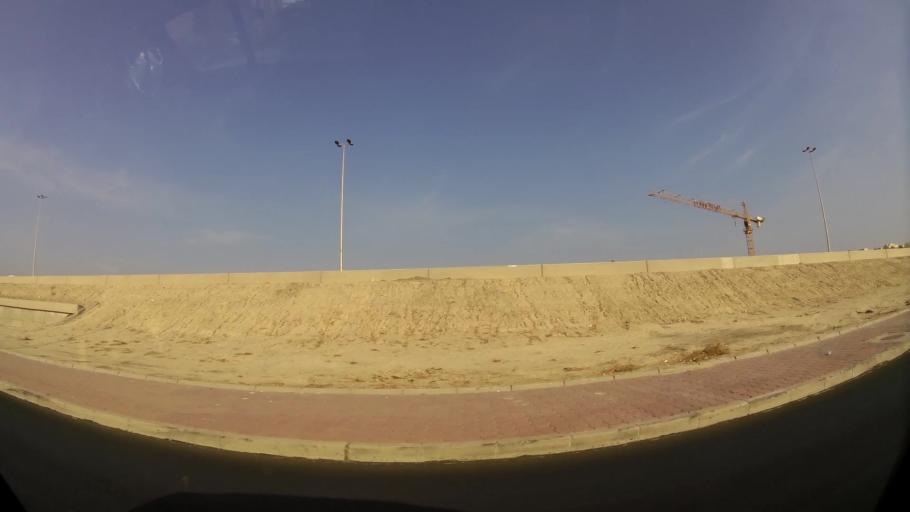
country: KW
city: Al Funaytis
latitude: 29.2095
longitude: 48.1037
